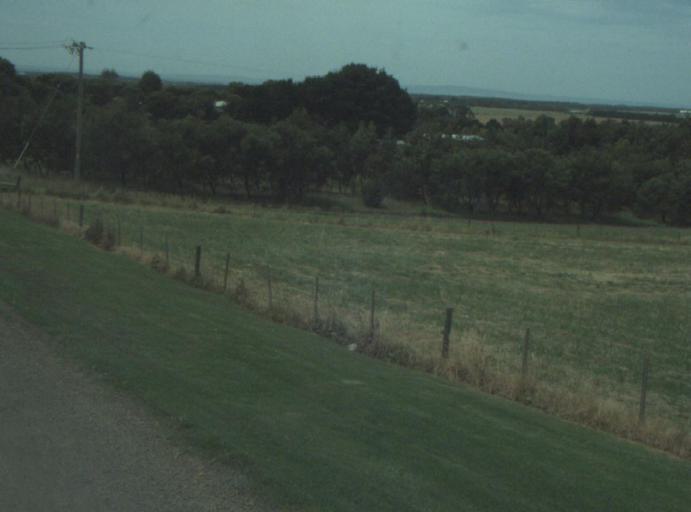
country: AU
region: Victoria
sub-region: Greater Geelong
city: Clifton Springs
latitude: -38.1239
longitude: 144.6448
